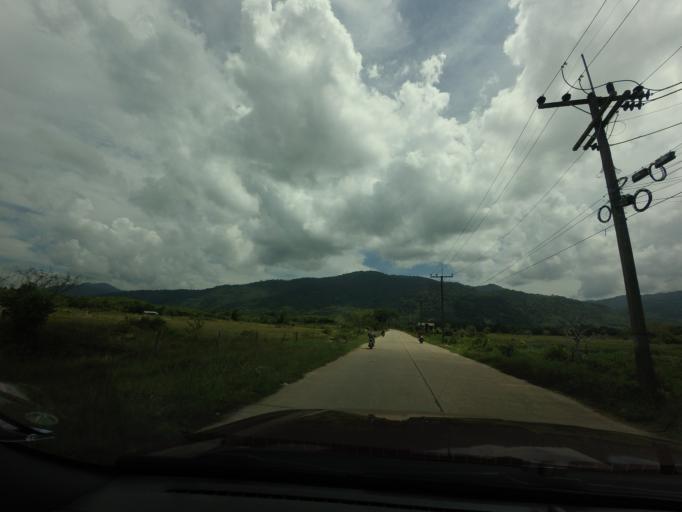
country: TH
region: Narathiwat
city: Bacho
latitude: 6.4879
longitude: 101.6643
